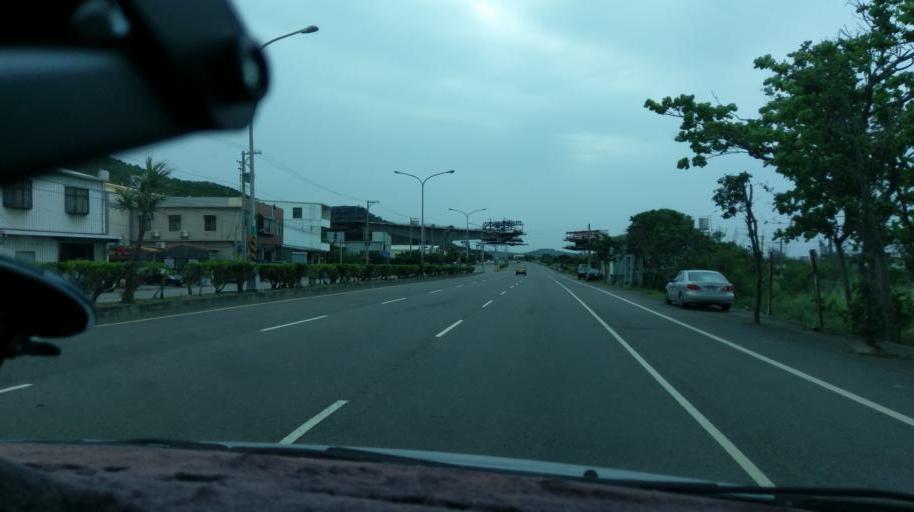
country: TW
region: Taiwan
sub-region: Miaoli
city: Miaoli
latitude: 24.5331
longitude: 120.6939
